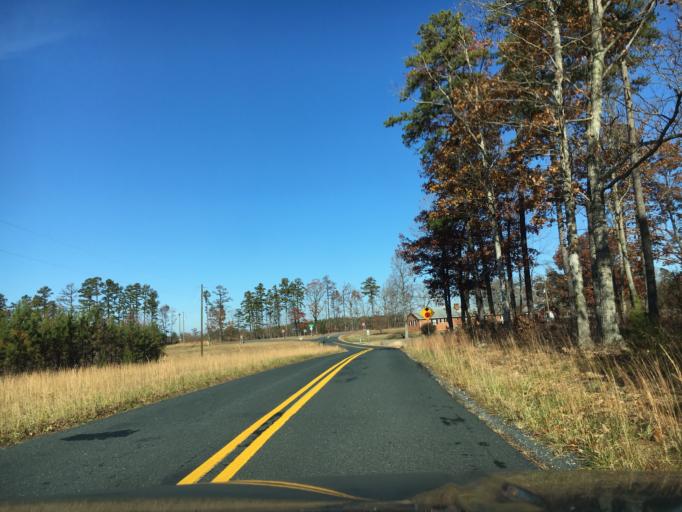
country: US
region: Virginia
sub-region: Buckingham County
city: Buckingham
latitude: 37.4564
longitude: -78.6798
